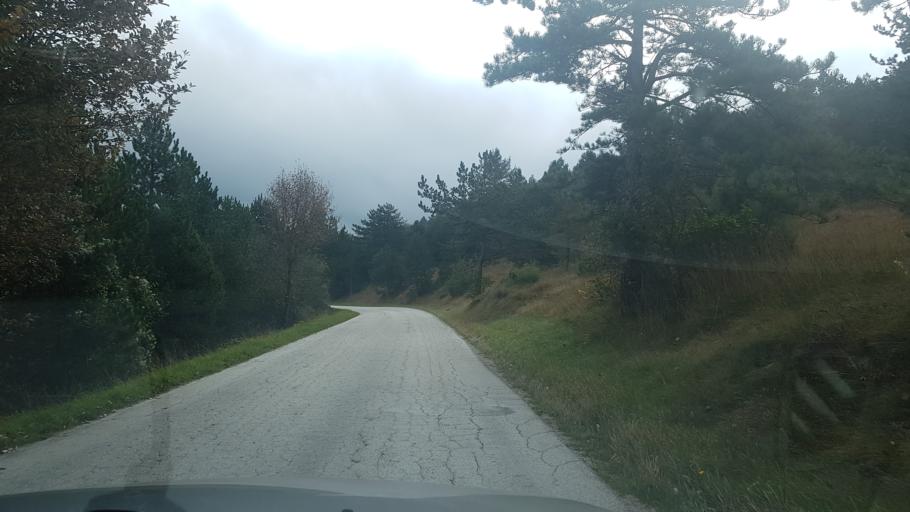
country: HR
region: Istarska
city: Buzet
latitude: 45.4954
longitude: 14.0233
